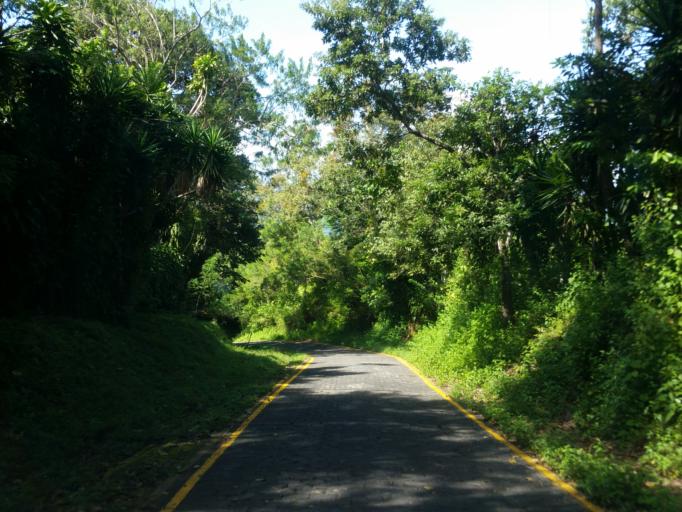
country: NI
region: Granada
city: Diriomo
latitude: 11.8403
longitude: -85.9989
